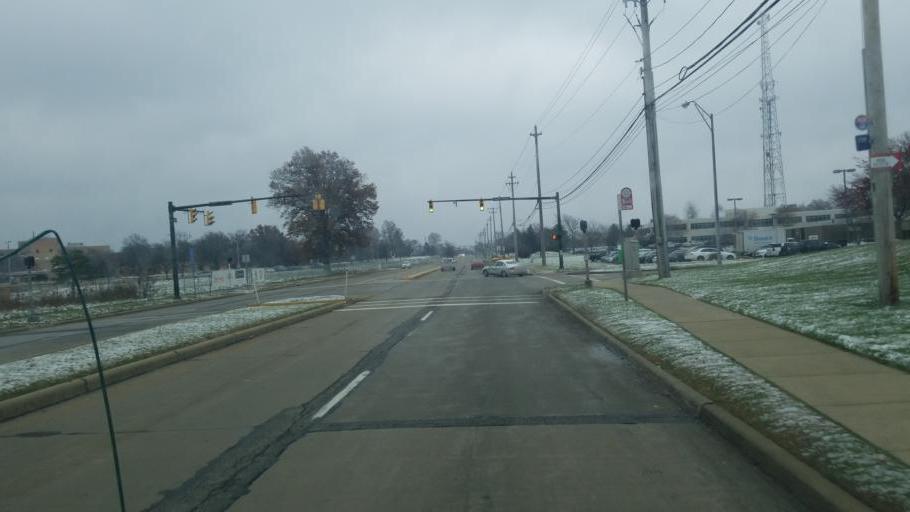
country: US
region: Ohio
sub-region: Cuyahoga County
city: Brecksville
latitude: 41.2893
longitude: -81.6338
